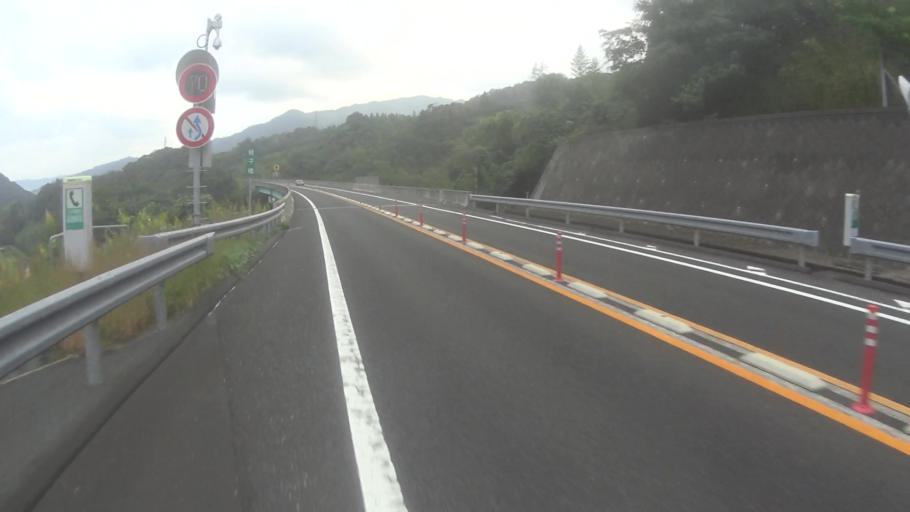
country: JP
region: Kyoto
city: Miyazu
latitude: 35.5002
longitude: 135.1780
